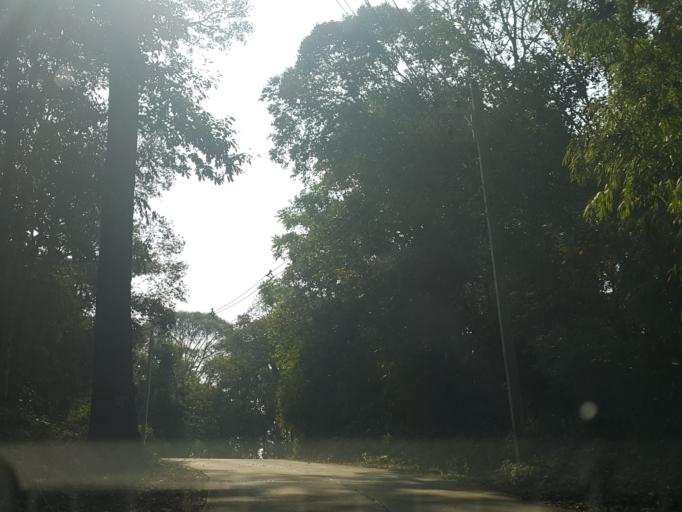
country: TH
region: Chiang Mai
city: Mae Taeng
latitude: 19.0242
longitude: 98.7842
